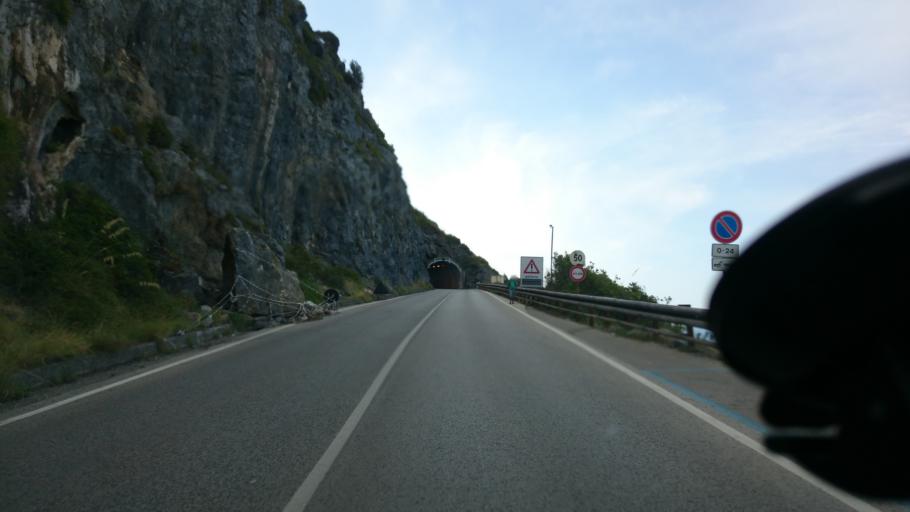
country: IT
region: Campania
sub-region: Provincia di Salerno
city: Marina di Camerota
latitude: 40.0093
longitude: 15.3396
